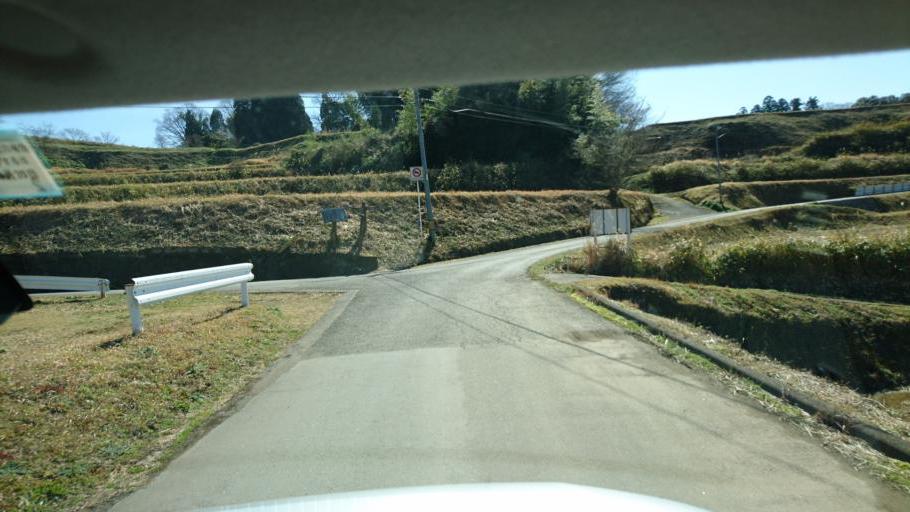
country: JP
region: Oita
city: Takedamachi
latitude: 32.7204
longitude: 131.3071
